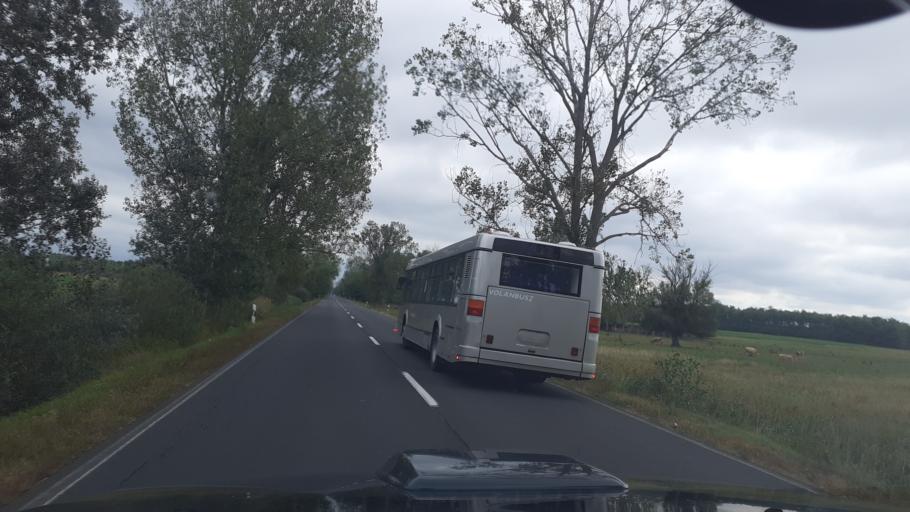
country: HU
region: Bacs-Kiskun
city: Agasegyhaza
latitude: 46.8764
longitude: 19.4780
